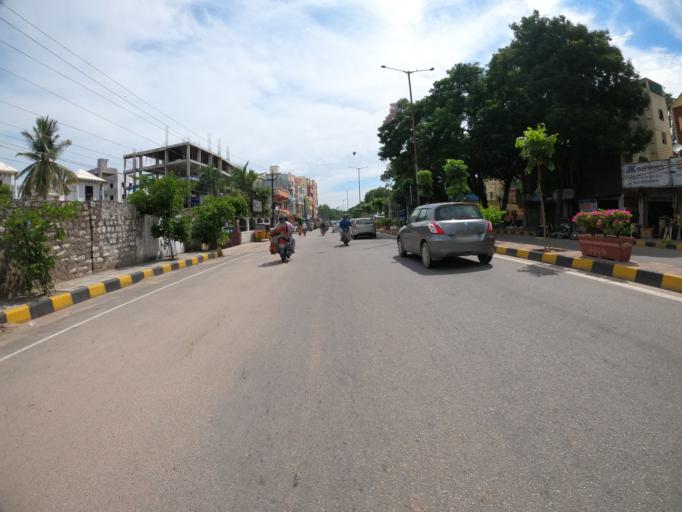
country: IN
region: Telangana
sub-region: Hyderabad
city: Hyderabad
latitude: 17.3928
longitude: 78.4254
